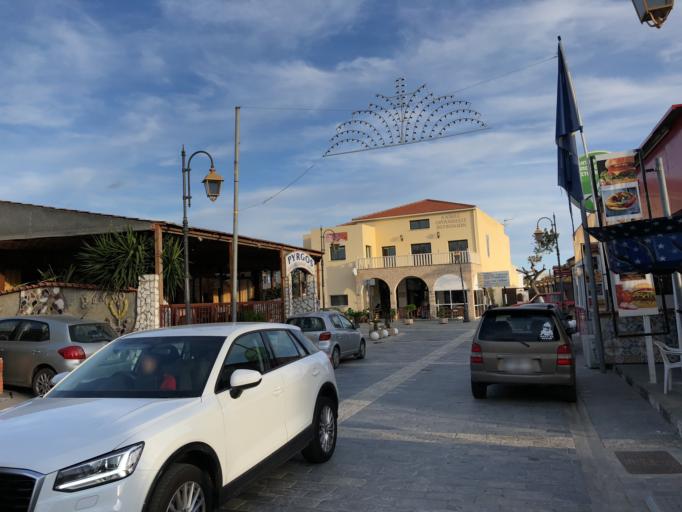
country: CY
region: Larnaka
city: Perivolia
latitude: 34.8290
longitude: 33.5796
